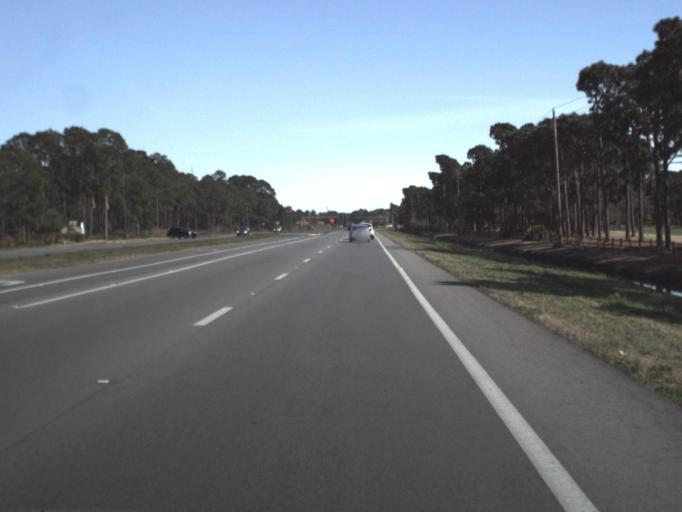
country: US
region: Florida
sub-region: Bay County
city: Panama City Beach
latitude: 30.1922
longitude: -85.7987
